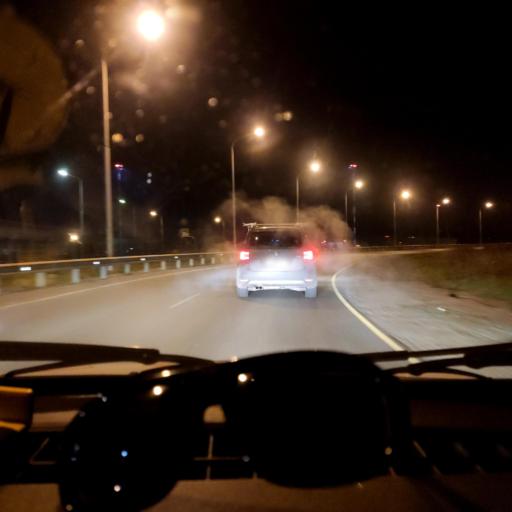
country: RU
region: Bashkortostan
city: Avdon
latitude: 54.5685
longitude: 55.8833
